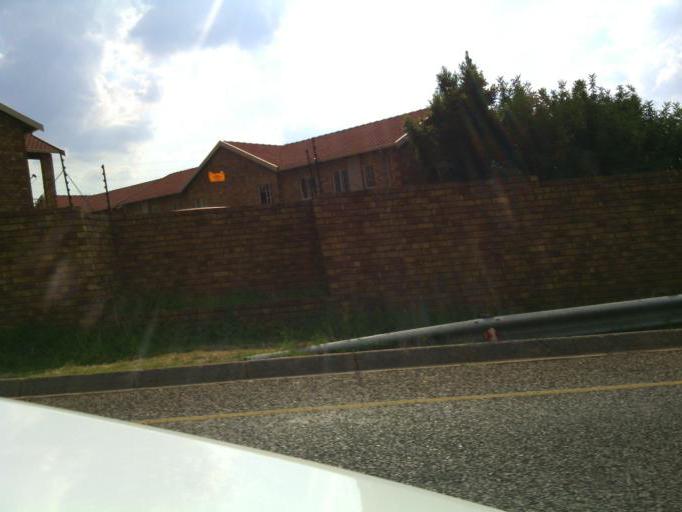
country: ZA
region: Gauteng
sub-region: City of Tshwane Metropolitan Municipality
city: Centurion
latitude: -25.8337
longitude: 28.1956
